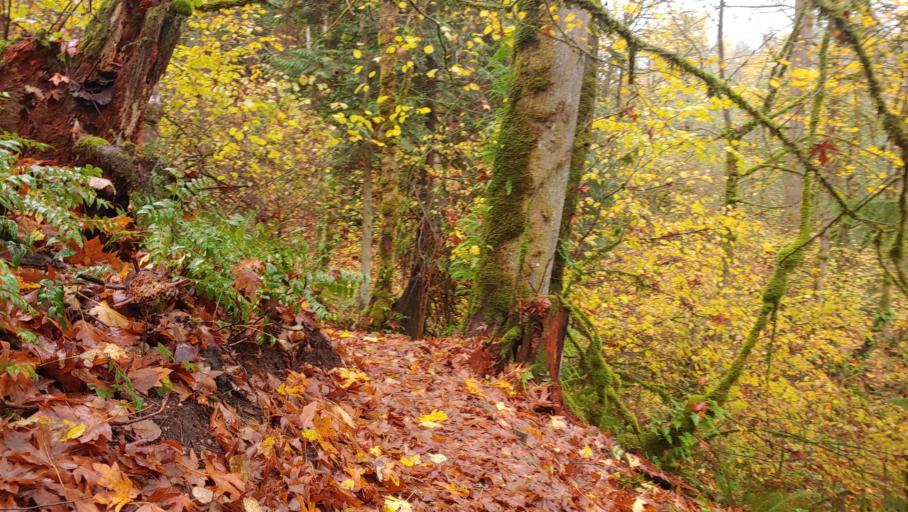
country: US
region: Washington
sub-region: King County
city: Newcastle
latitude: 47.5518
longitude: -122.1639
